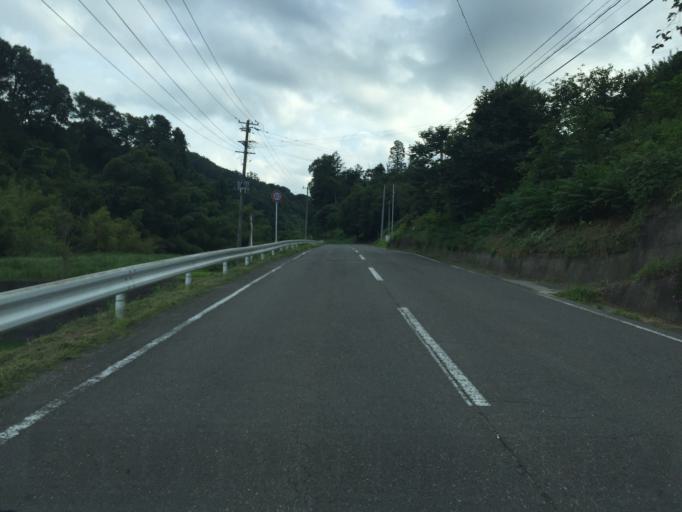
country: JP
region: Fukushima
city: Hobaramachi
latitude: 37.7125
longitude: 140.5866
